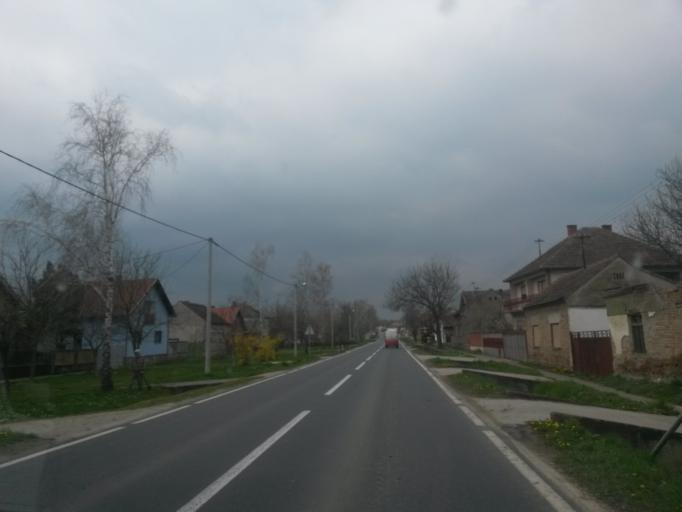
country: HR
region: Vukovarsko-Srijemska
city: Slakovci
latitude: 45.2141
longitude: 18.9880
